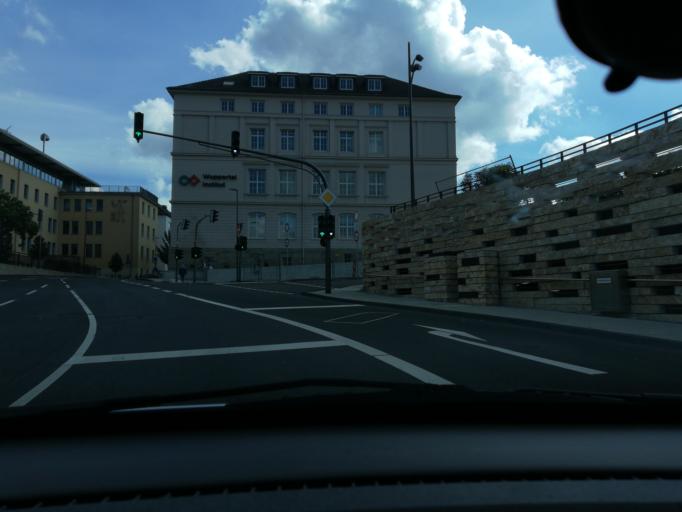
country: DE
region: North Rhine-Westphalia
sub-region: Regierungsbezirk Dusseldorf
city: Wuppertal
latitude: 51.2554
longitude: 7.1514
